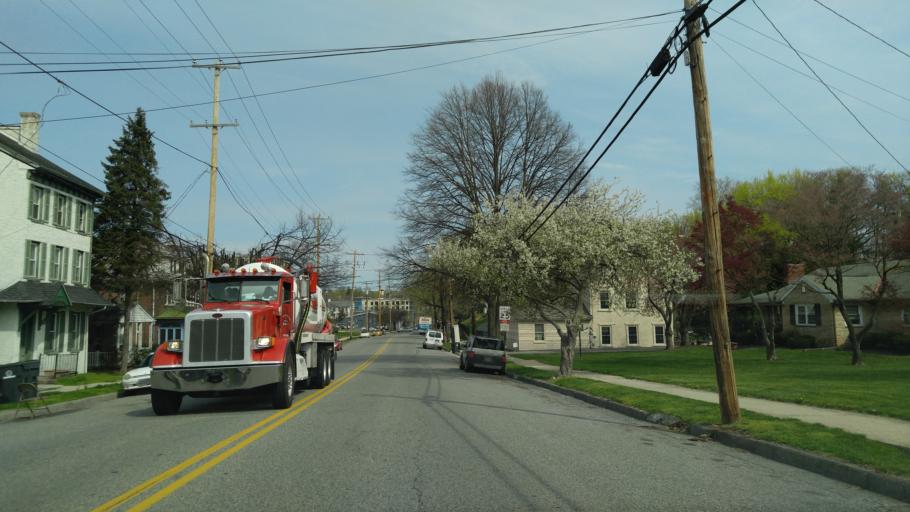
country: US
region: Pennsylvania
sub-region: Chester County
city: Phoenixville
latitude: 40.1316
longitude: -75.5116
